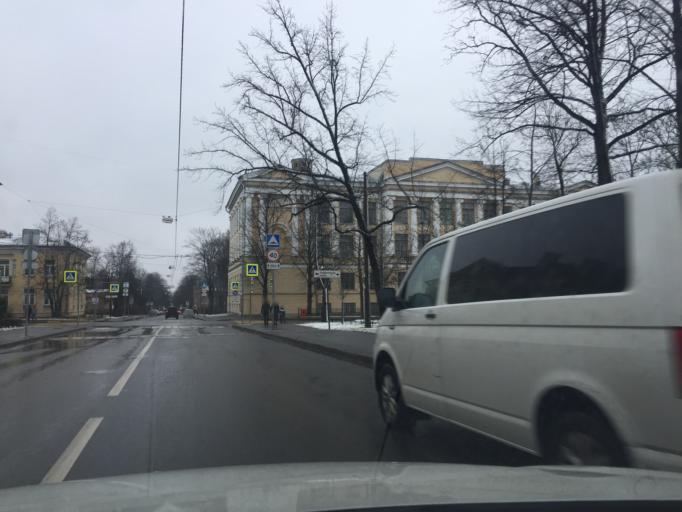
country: RU
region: St.-Petersburg
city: Pushkin
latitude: 59.7213
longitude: 30.4056
